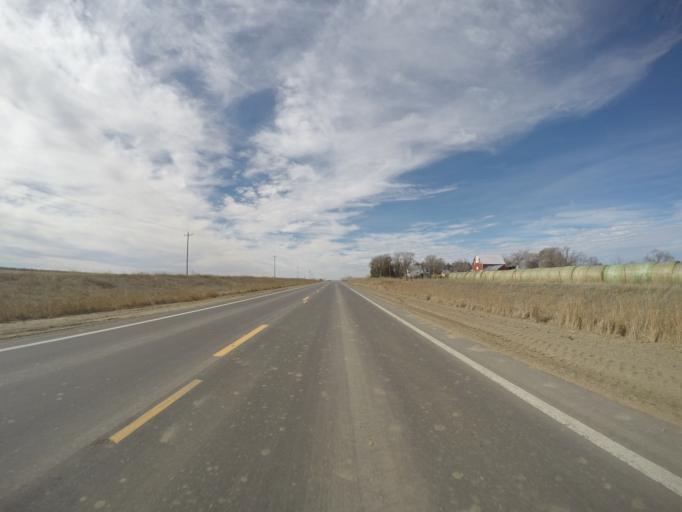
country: US
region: Nebraska
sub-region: Franklin County
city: Franklin
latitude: 40.0970
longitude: -98.8119
